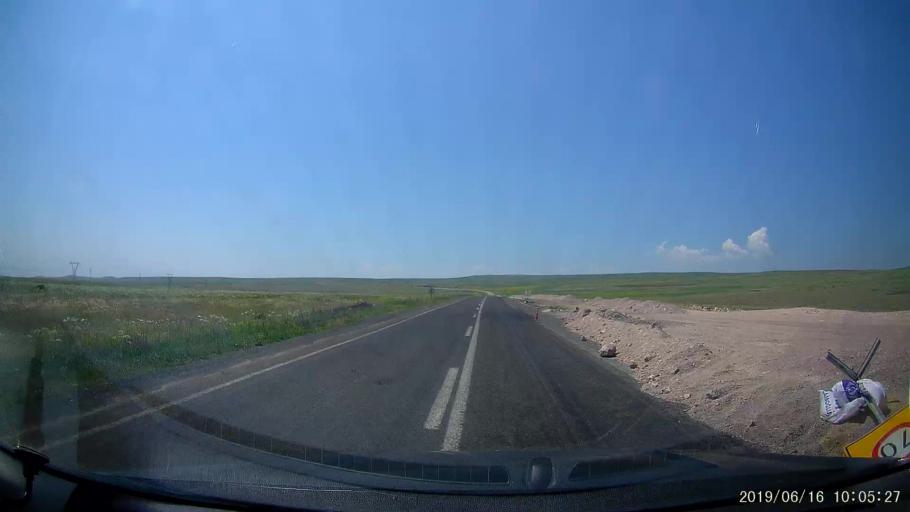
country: TR
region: Kars
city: Digor
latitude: 40.2701
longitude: 43.5385
